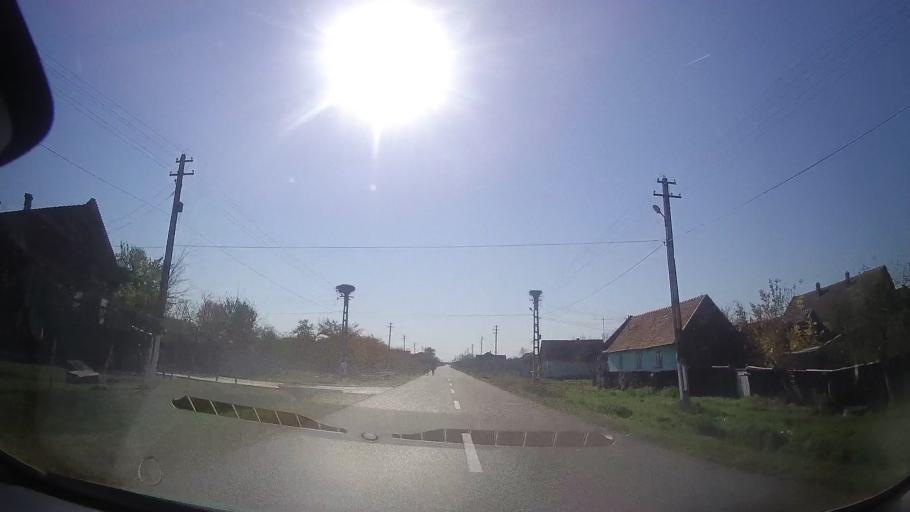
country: RO
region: Timis
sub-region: Comuna Ghizela
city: Ghizela
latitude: 45.7974
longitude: 21.7266
